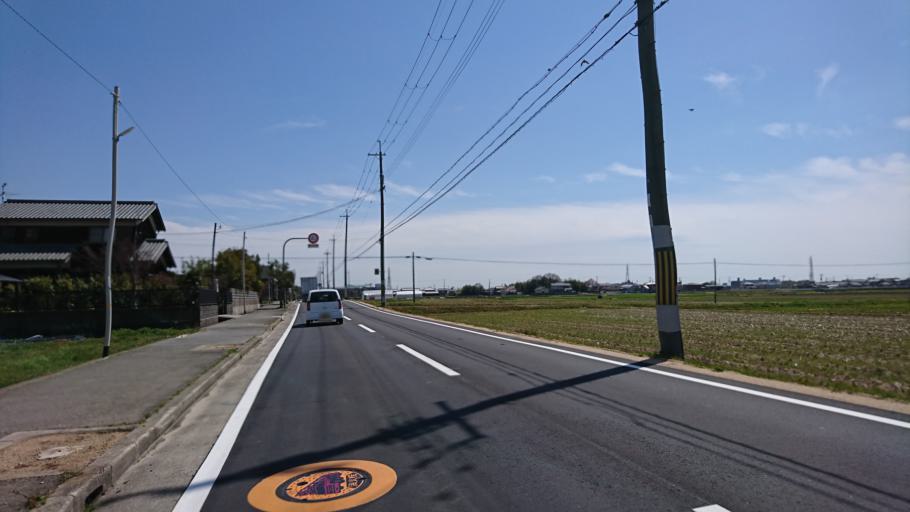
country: JP
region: Hyogo
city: Kakogawacho-honmachi
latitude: 34.7382
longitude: 134.8957
